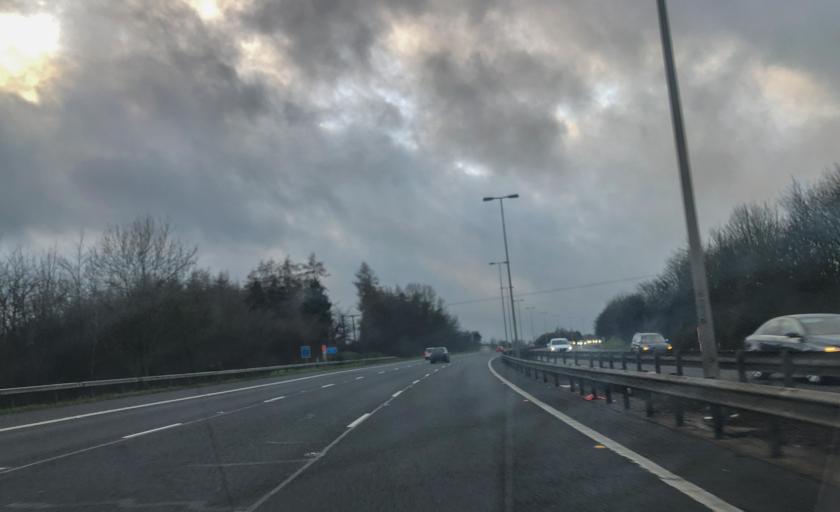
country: GB
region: England
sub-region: Buckinghamshire
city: Stokenchurch
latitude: 51.6248
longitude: -0.8382
